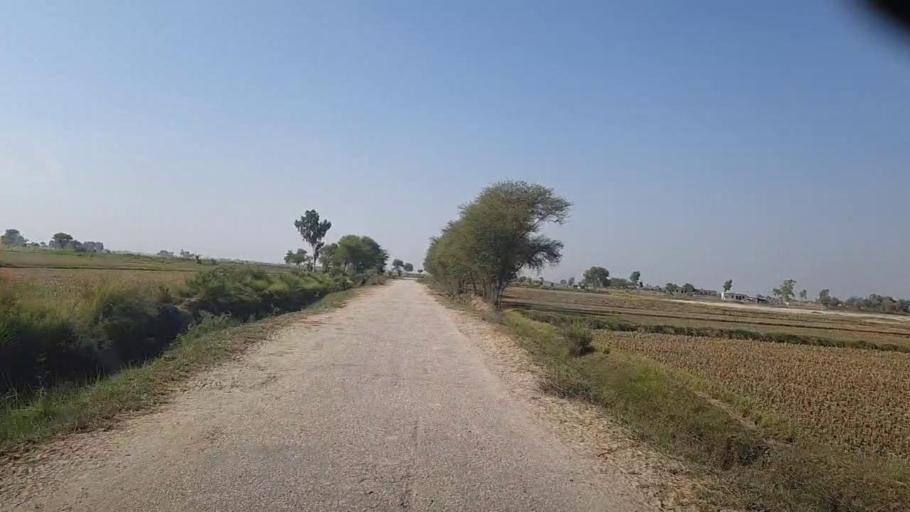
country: PK
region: Sindh
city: Tangwani
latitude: 28.2465
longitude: 68.9475
